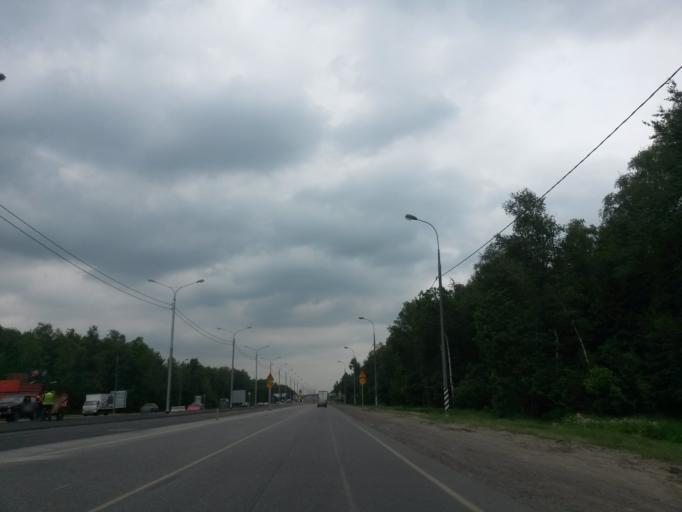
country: RU
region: Moskovskaya
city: Lyubuchany
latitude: 55.1936
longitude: 37.5348
